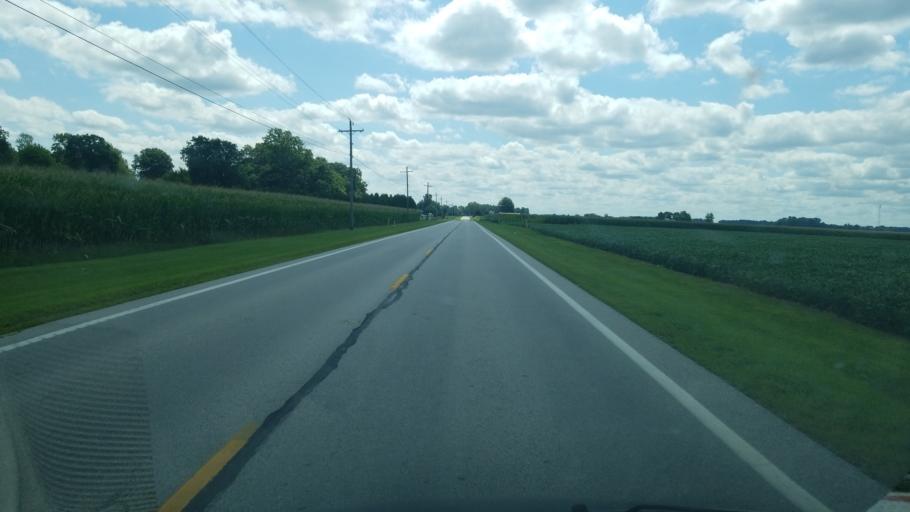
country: US
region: Ohio
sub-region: Fulton County
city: Delta
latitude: 41.5248
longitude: -84.0037
